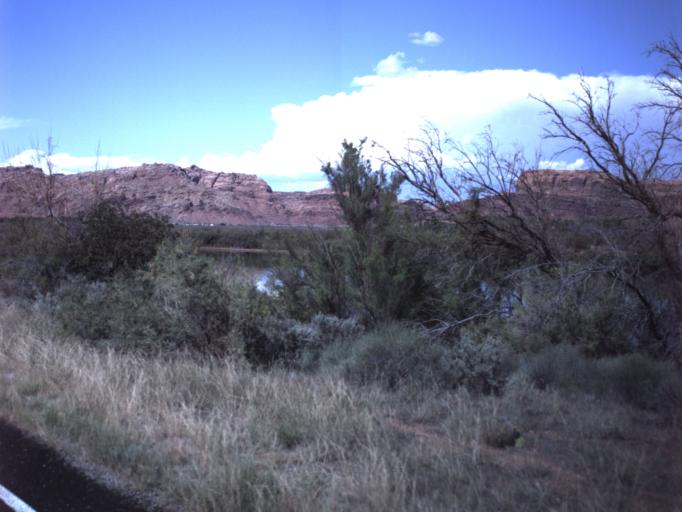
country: US
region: Utah
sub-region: Grand County
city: Moab
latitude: 38.5773
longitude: -109.5838
